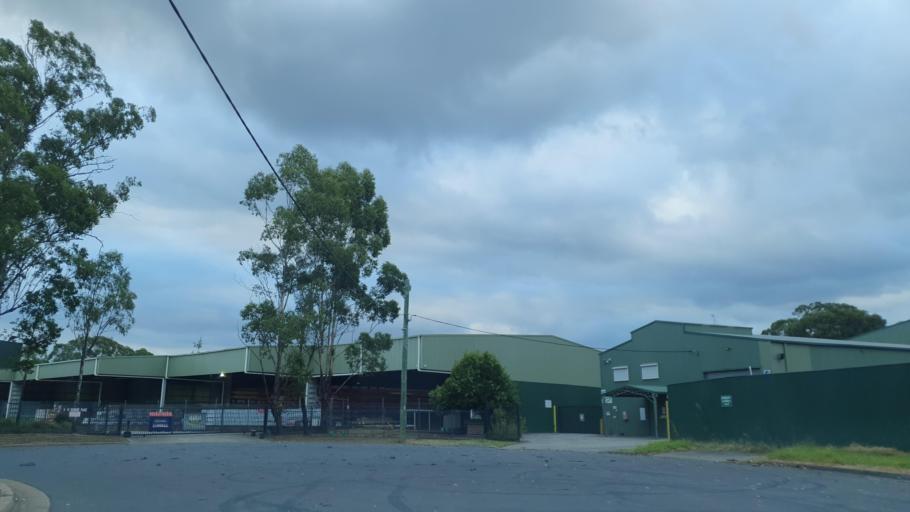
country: AU
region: New South Wales
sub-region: Penrith Municipality
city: Werrington County
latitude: -33.7408
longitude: 150.7651
